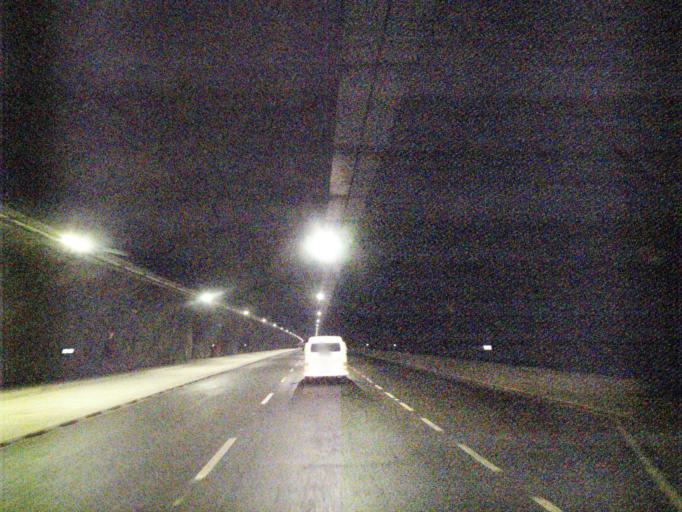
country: BR
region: Rio de Janeiro
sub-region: Niteroi
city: Niteroi
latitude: -22.9349
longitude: -43.0907
